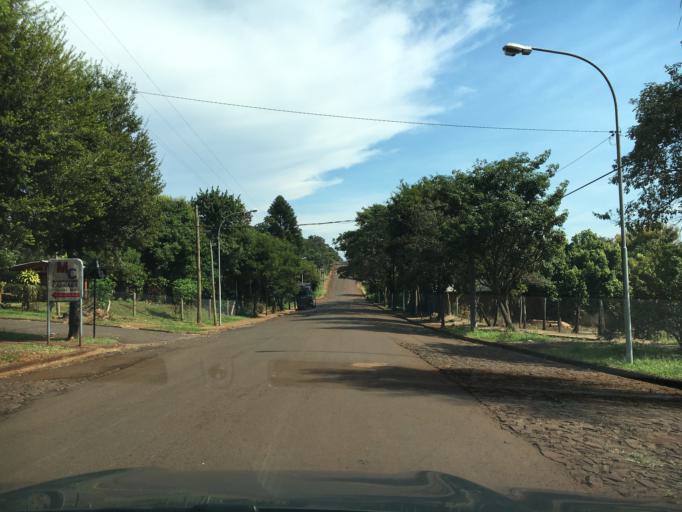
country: AR
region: Misiones
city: Puerto Rico
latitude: -26.8064
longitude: -55.0159
